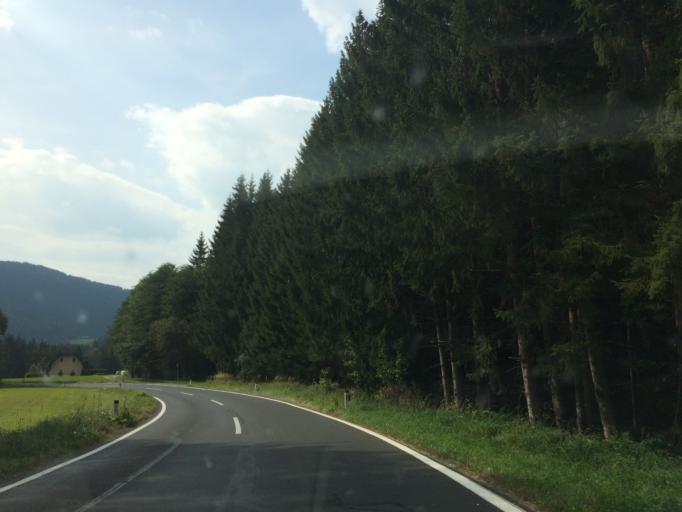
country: AT
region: Styria
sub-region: Politischer Bezirk Murtal
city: Seckau
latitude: 47.2717
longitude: 14.8166
